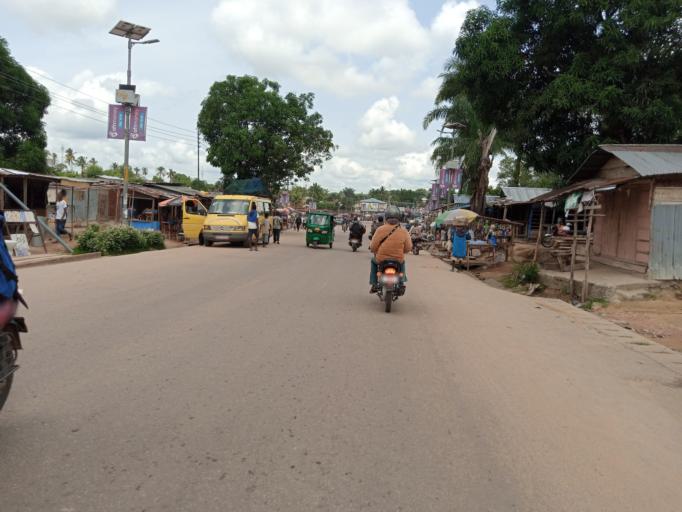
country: SL
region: Southern Province
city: Bo
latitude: 7.9453
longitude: -11.7272
